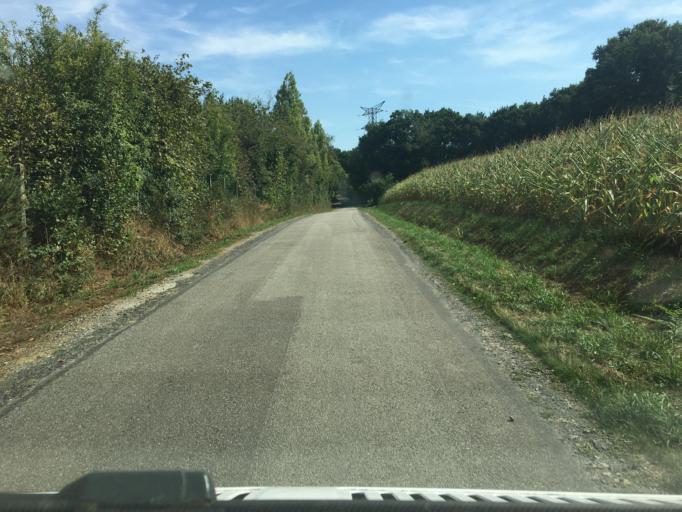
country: FR
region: Brittany
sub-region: Departement des Cotes-d'Armor
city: Mur-de-Bretagne
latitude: 48.2064
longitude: -3.0049
